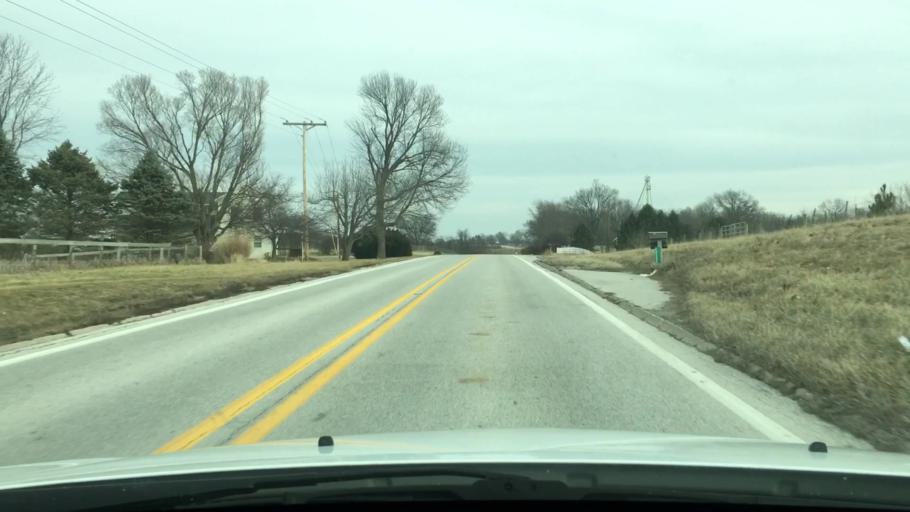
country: US
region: Missouri
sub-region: Pike County
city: Louisiana
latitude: 39.5242
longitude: -90.9398
